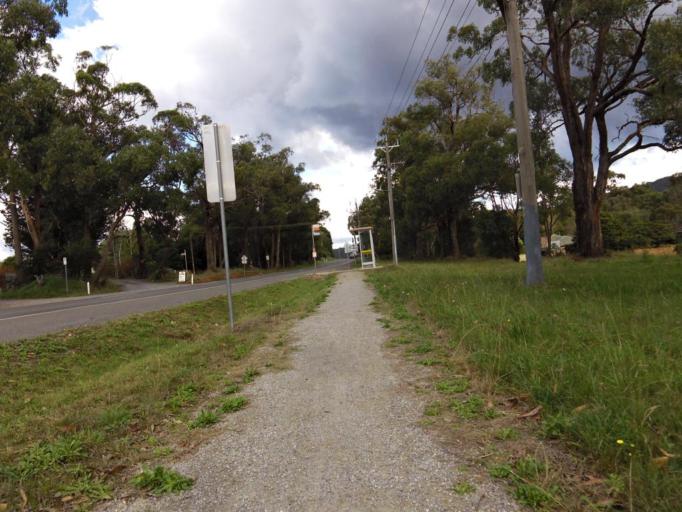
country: AU
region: Victoria
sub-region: Yarra Ranges
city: Mount Evelyn
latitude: -37.7918
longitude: 145.3886
